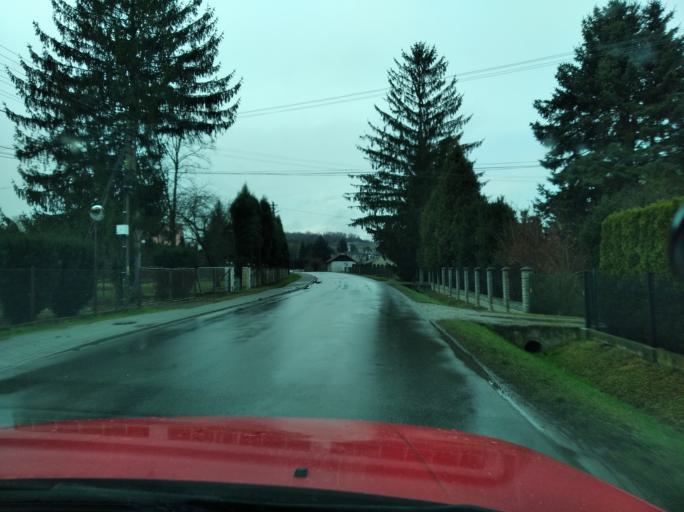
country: PL
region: Subcarpathian Voivodeship
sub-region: Powiat rzeszowski
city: Lutoryz
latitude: 49.9507
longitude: 21.9210
